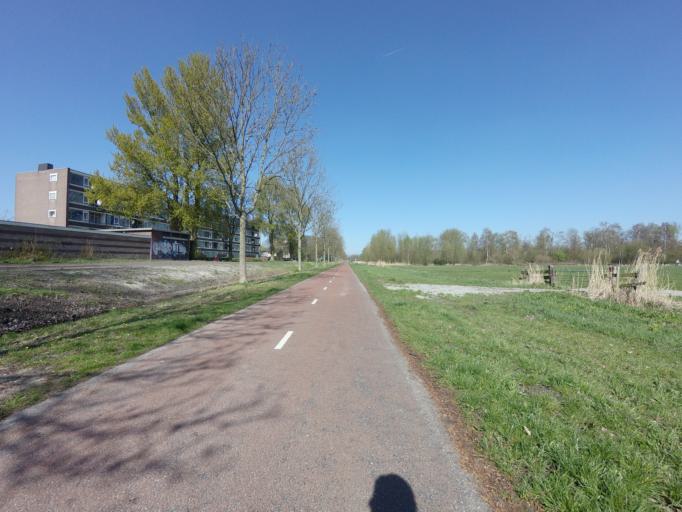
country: NL
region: North Holland
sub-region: Gemeente Haarlem
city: Haarlem
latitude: 52.3611
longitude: 4.6677
